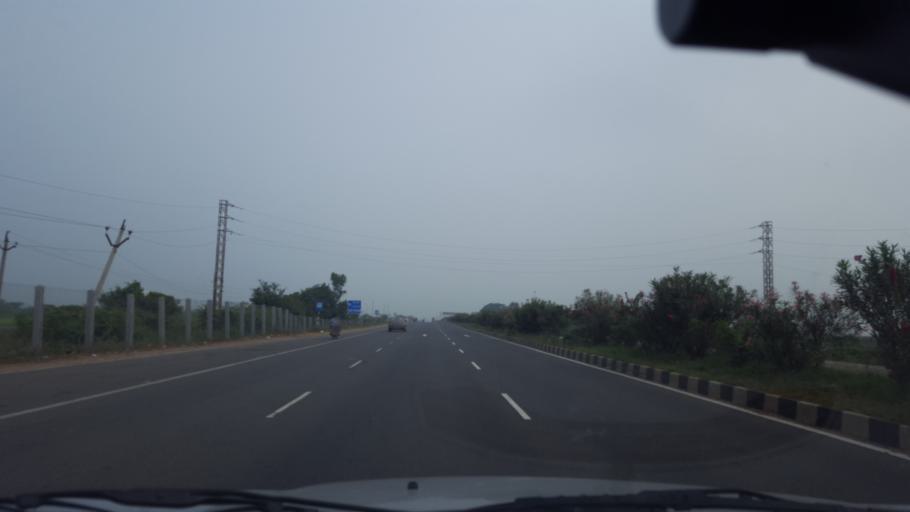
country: IN
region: Andhra Pradesh
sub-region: Guntur
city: Chilakalurupet
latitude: 16.0071
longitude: 80.1149
